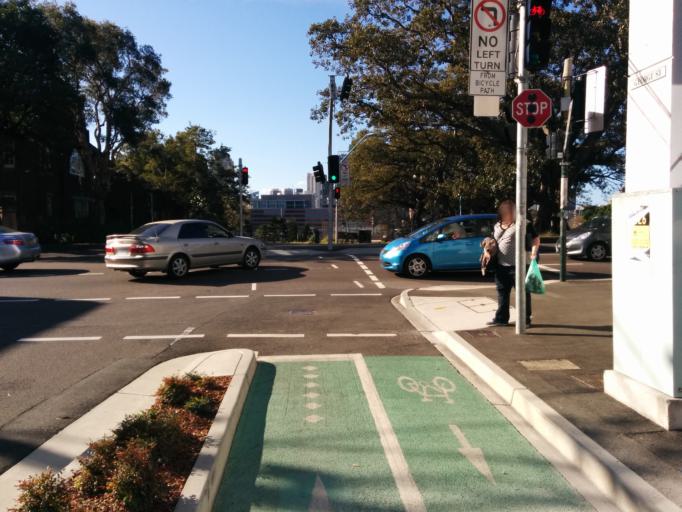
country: AU
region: New South Wales
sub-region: City of Sydney
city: Redfern
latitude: -33.8895
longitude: 151.2028
